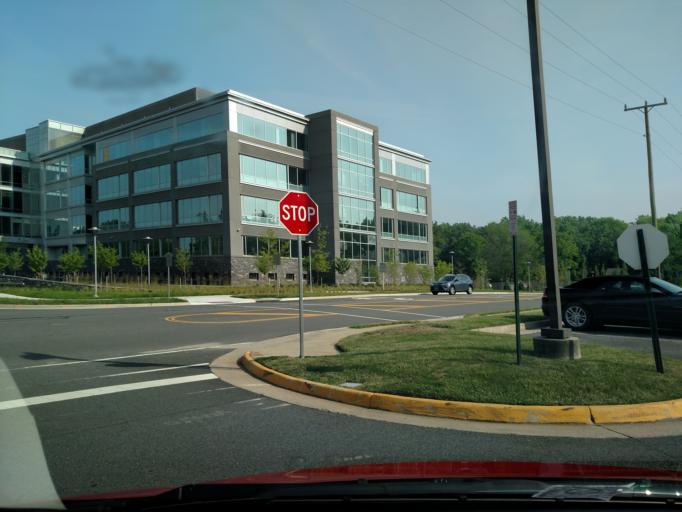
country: US
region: Virginia
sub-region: Fairfax County
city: Merrifield
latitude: 38.8643
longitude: -77.2347
